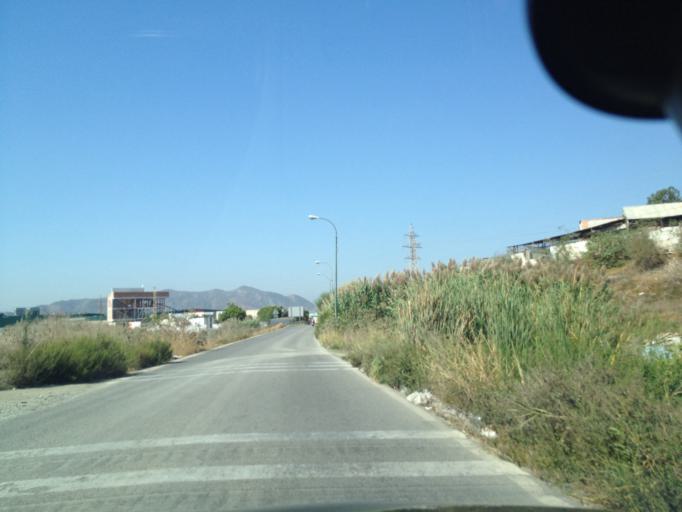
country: ES
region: Andalusia
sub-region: Provincia de Malaga
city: Alhaurin de la Torre
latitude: 36.7189
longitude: -4.5261
